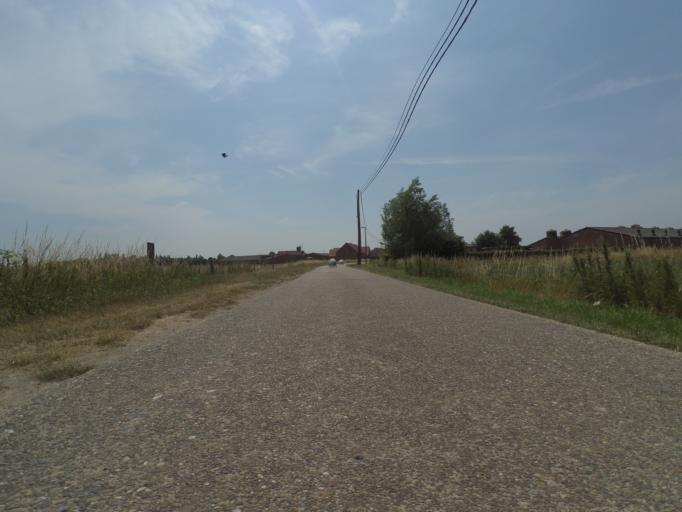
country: BE
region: Flanders
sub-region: Provincie Antwerpen
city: Brecht
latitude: 51.3869
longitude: 4.6332
